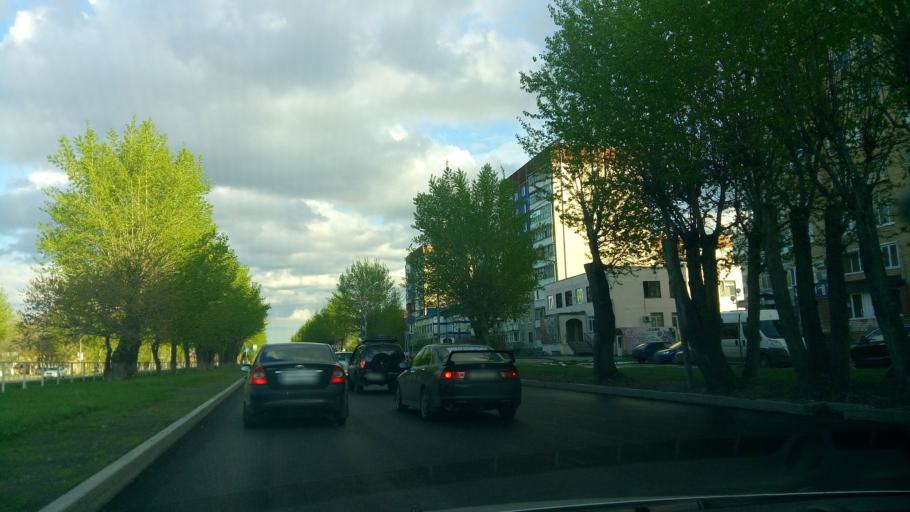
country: RU
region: Tjumen
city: Tyumen
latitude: 57.1366
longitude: 65.5985
